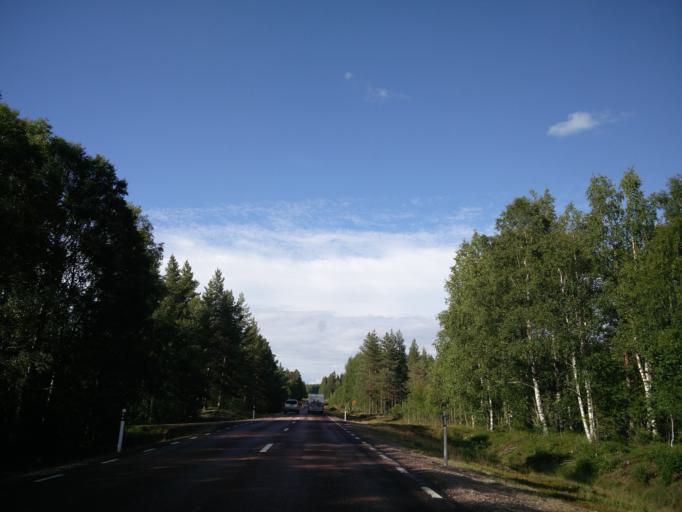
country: SE
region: Vaermland
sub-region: Hagfors Kommun
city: Ekshaerad
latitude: 60.4679
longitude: 13.3015
